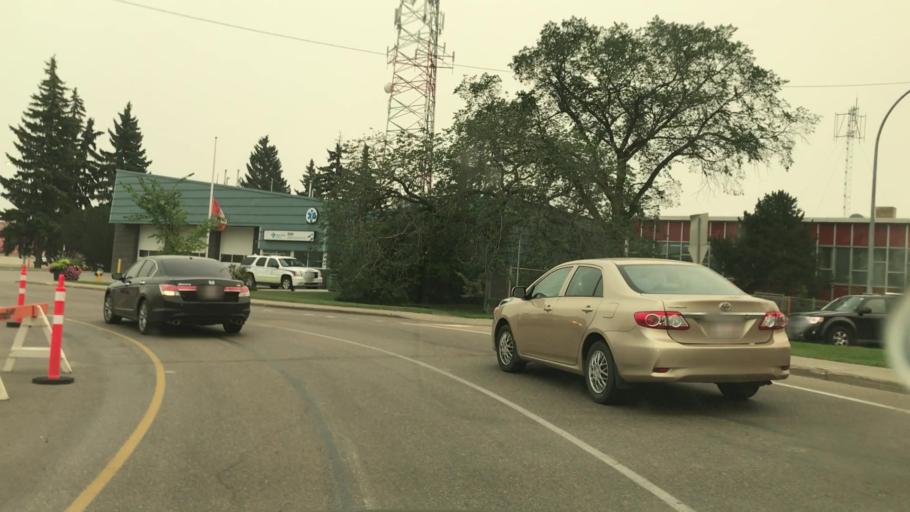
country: CA
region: Alberta
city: Edmonton
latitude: 53.5247
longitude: -113.4581
